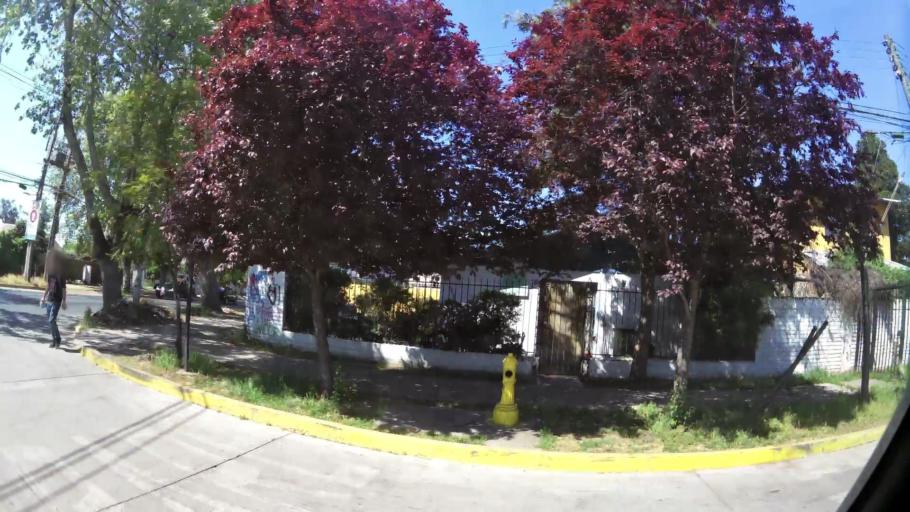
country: CL
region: Santiago Metropolitan
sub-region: Provincia de Talagante
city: Penaflor
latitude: -33.6118
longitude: -70.8976
